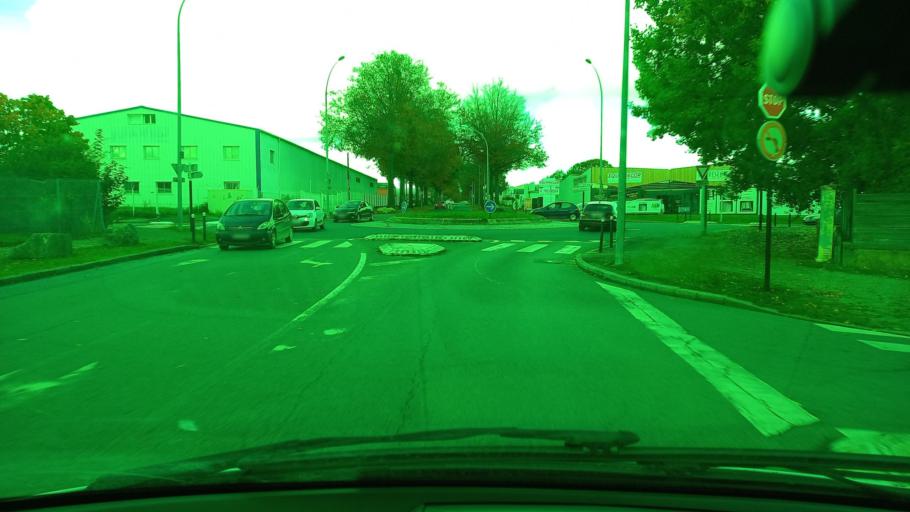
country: FR
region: Pays de la Loire
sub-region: Departement de la Loire-Atlantique
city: Sainte-Luce-sur-Loire
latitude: 47.2501
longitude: -1.4971
